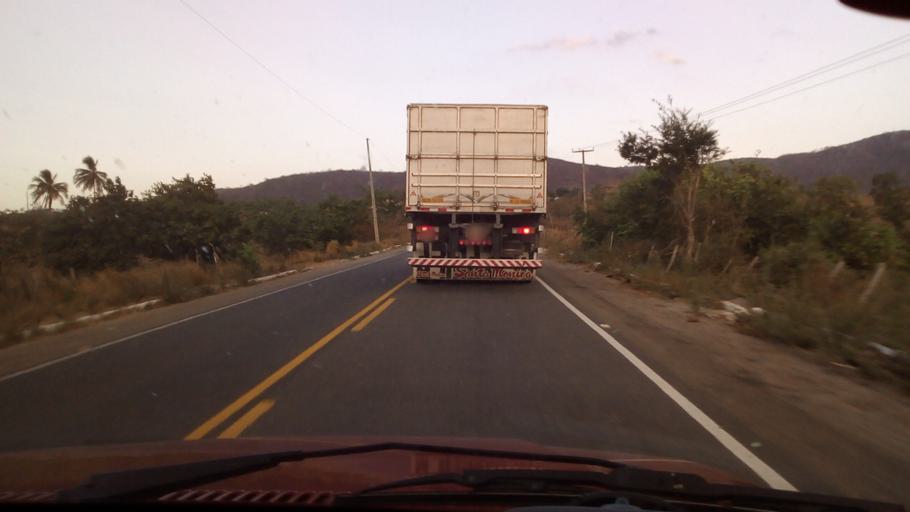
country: BR
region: Paraiba
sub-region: Bananeiras
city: Solanea
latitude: -6.7224
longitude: -35.5483
